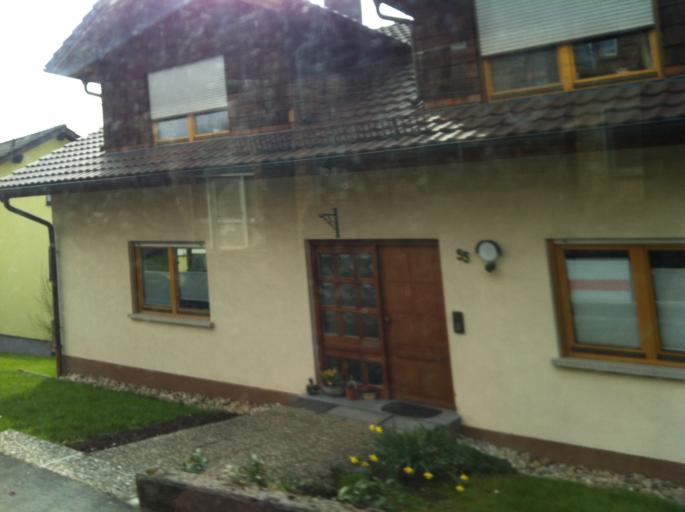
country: DE
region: Baden-Wuerttemberg
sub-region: Karlsruhe Region
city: Fahrenbach
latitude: 49.4420
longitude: 9.1629
